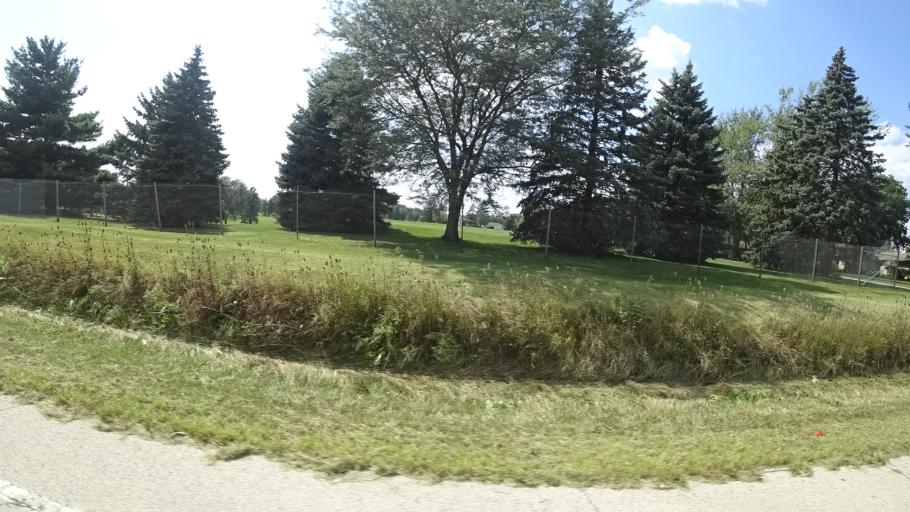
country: US
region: Illinois
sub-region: Cook County
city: Orland Park
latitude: 41.6255
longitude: -87.8195
